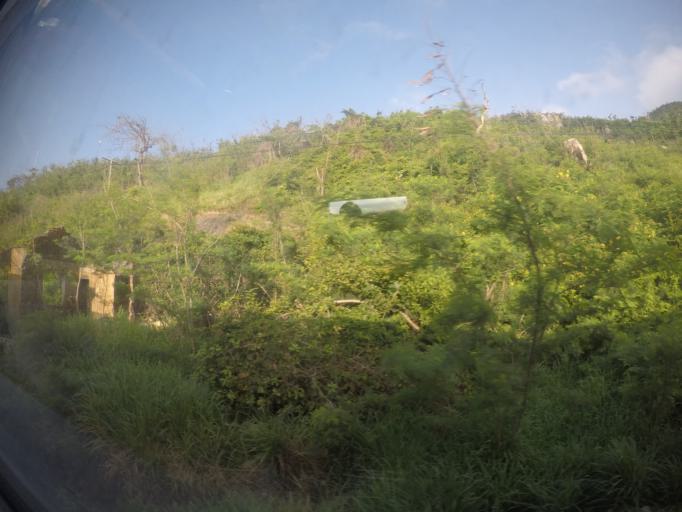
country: VN
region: Khanh Hoa
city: Van Gia
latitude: 12.8475
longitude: 109.3903
